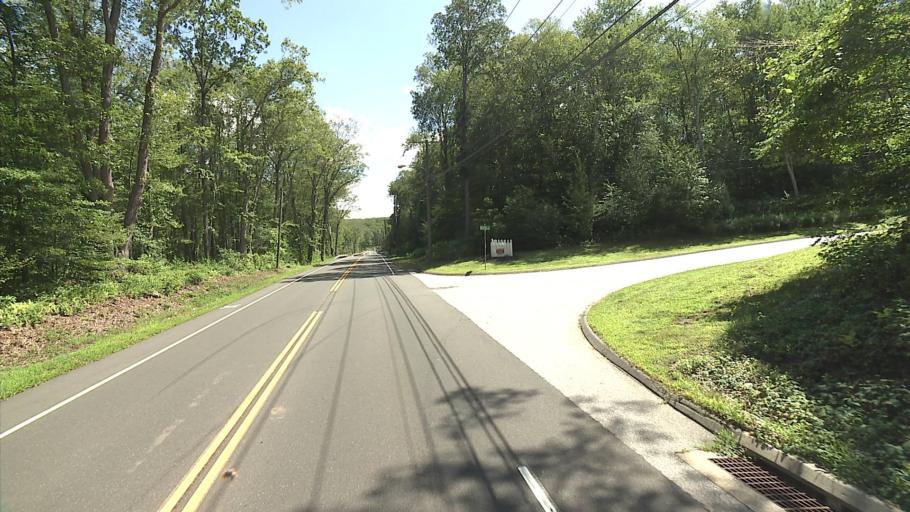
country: US
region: Connecticut
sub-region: New London County
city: Niantic
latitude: 41.3490
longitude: -72.2780
